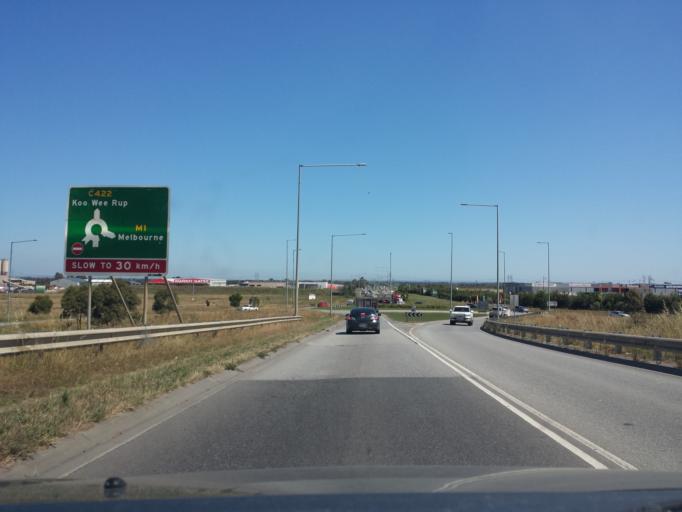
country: AU
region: Victoria
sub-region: Cardinia
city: Pakenham South
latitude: -38.0928
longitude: 145.4901
